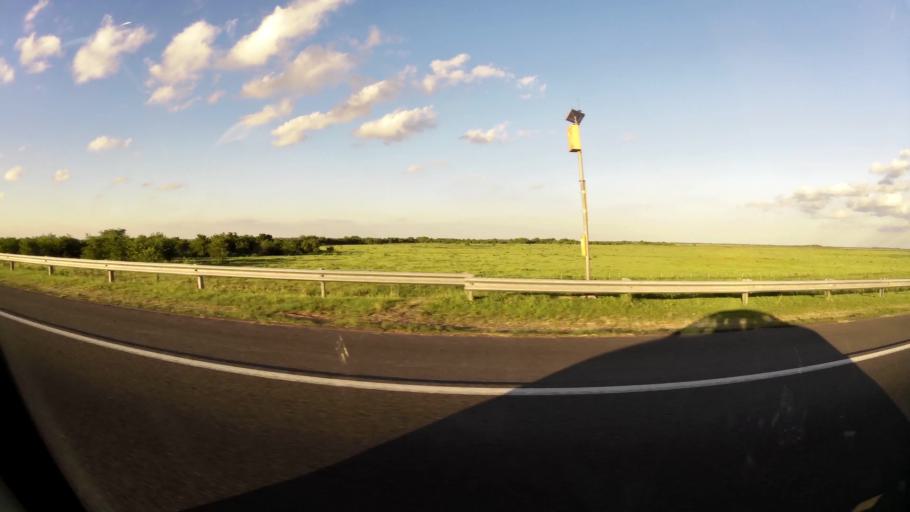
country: AR
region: Buenos Aires
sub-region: Partido de Quilmes
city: Quilmes
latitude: -34.8208
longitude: -58.1029
